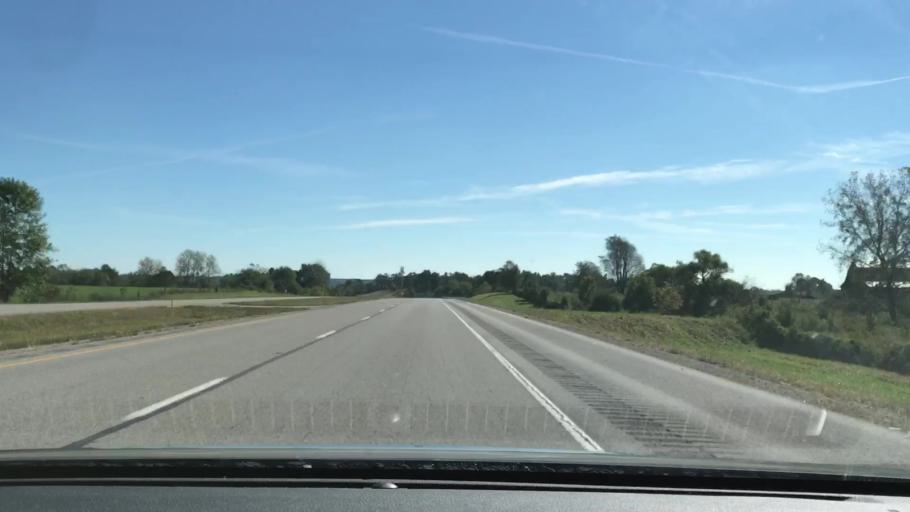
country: US
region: Kentucky
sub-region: Todd County
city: Elkton
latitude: 36.8221
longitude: -87.1962
